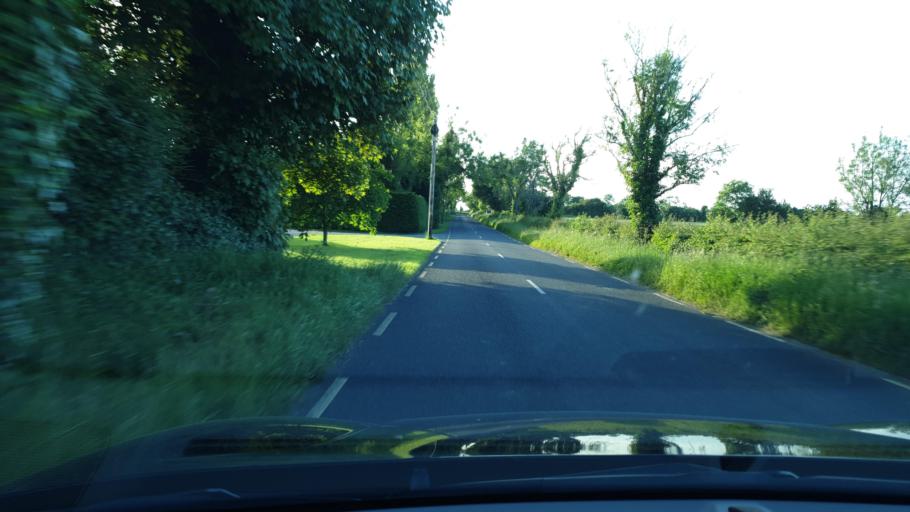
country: IE
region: Leinster
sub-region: An Mhi
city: Ashbourne
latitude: 53.4767
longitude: -6.4264
